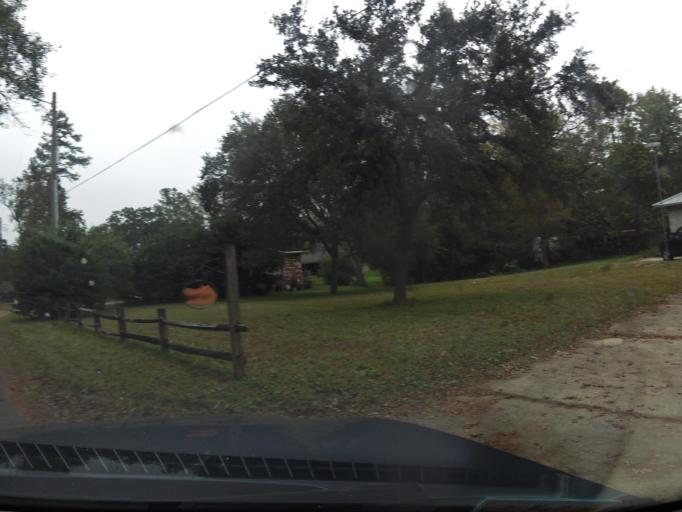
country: US
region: Florida
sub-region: Duval County
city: Jacksonville
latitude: 30.2757
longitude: -81.5888
